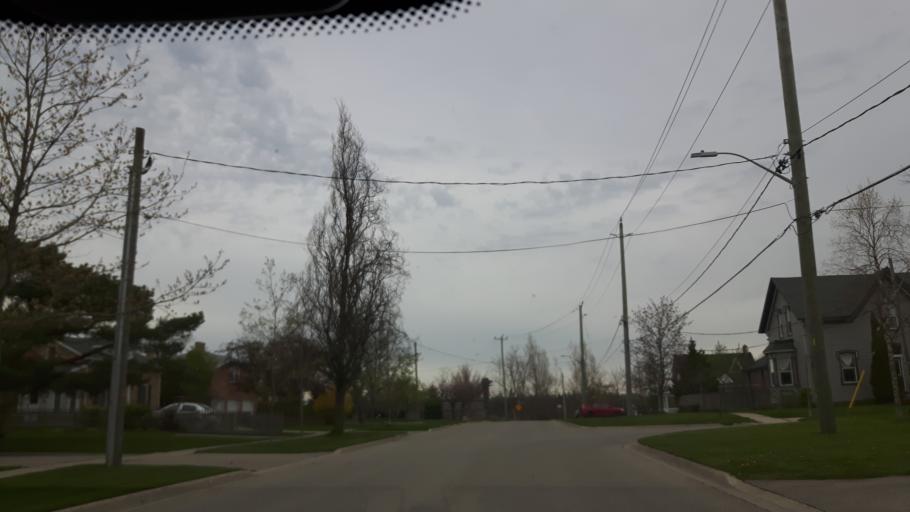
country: CA
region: Ontario
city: Goderich
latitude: 43.7436
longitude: -81.7178
